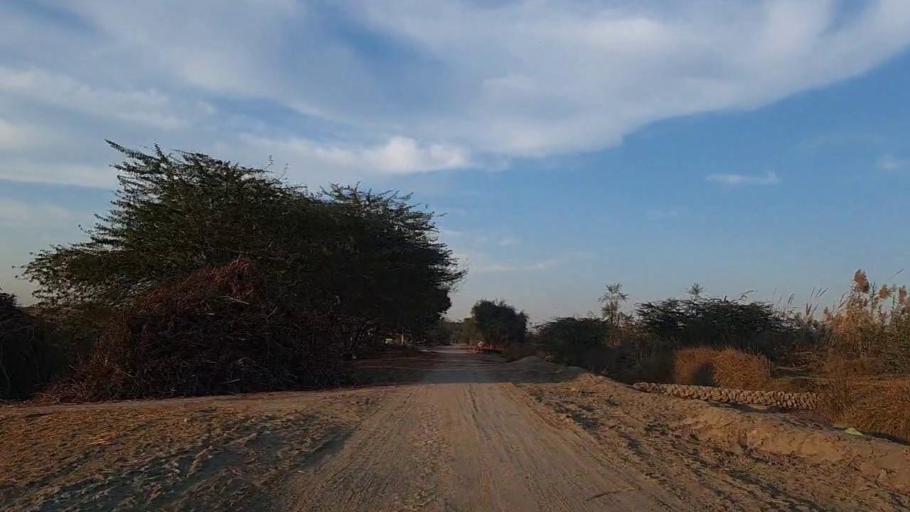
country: PK
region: Sindh
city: Bandhi
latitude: 26.6070
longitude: 68.3592
